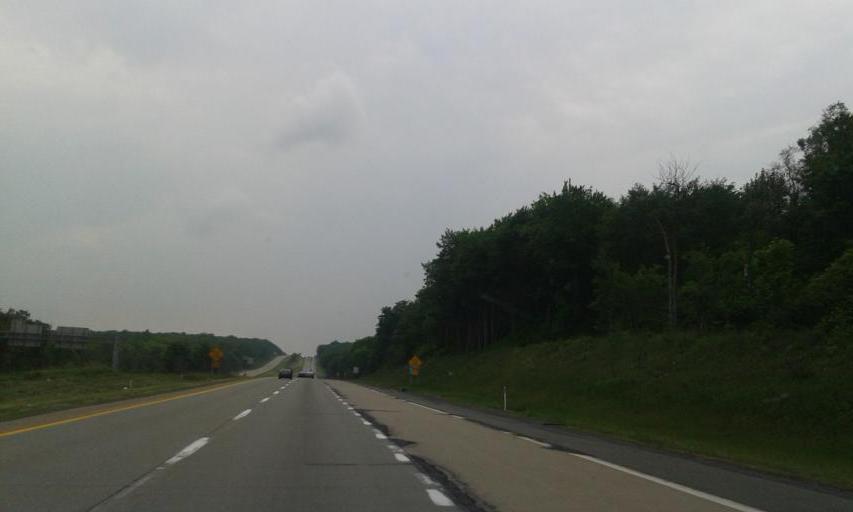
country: US
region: Pennsylvania
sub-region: Monroe County
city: Pocono Pines
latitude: 41.1875
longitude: -75.4385
